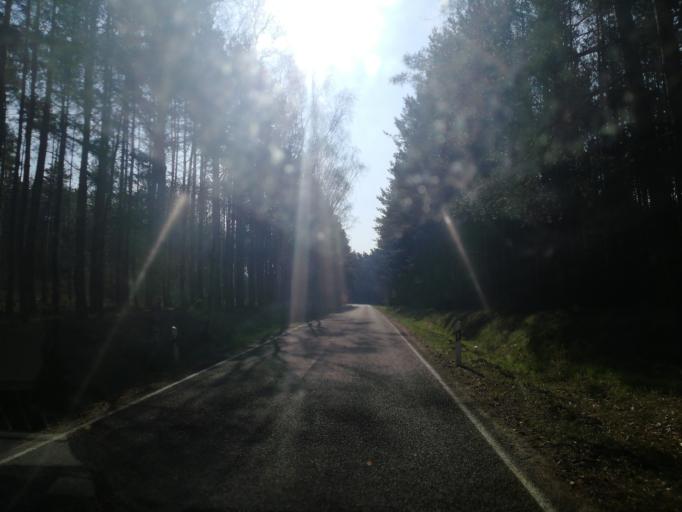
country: DE
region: Brandenburg
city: Sonnewalde
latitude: 51.7736
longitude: 13.6392
